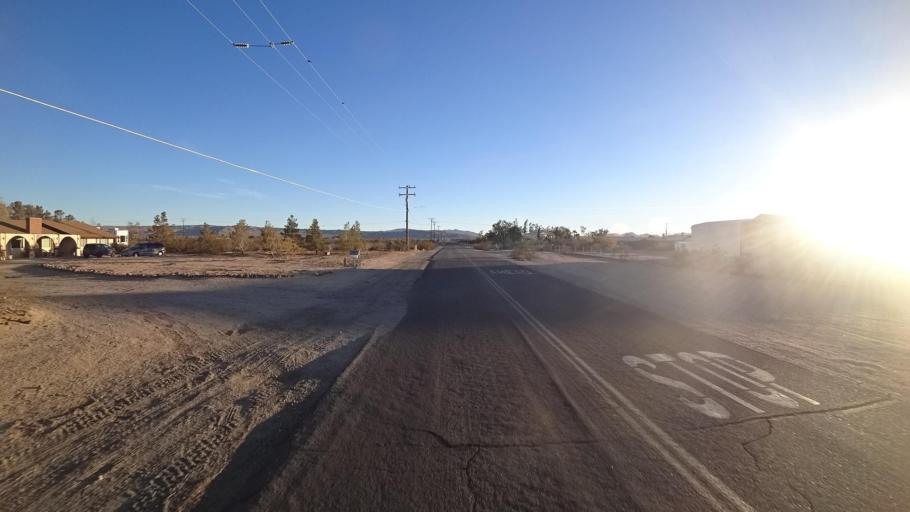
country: US
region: California
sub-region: Kern County
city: Ridgecrest
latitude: 35.6313
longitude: -117.7054
